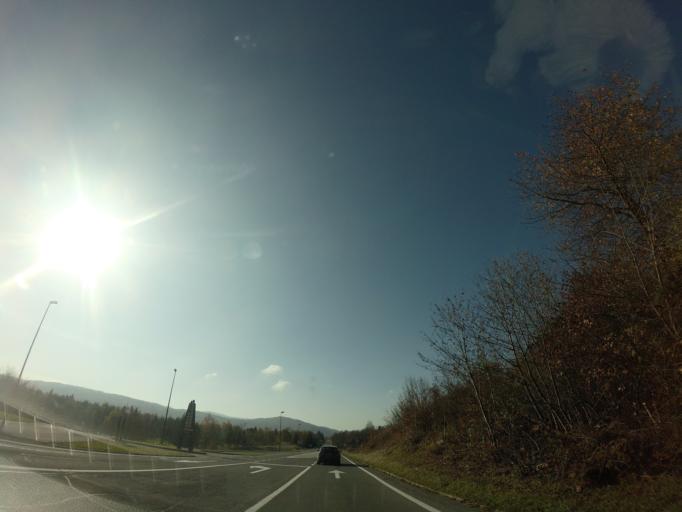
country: HR
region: Licko-Senjska
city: Jezerce
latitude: 44.9524
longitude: 15.6401
